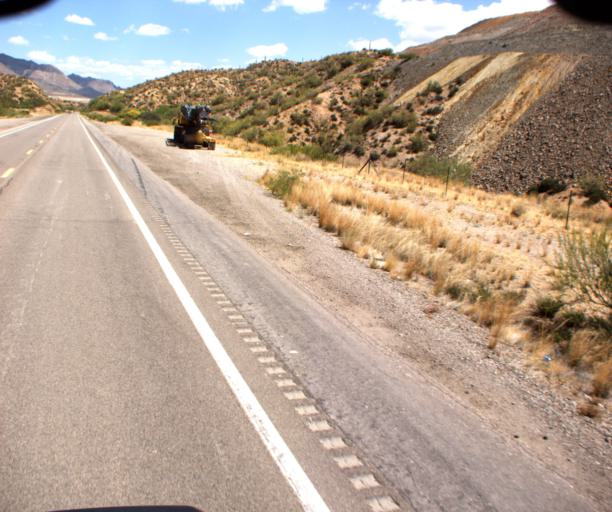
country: US
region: Arizona
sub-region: Pinal County
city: Kearny
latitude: 33.1499
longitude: -110.9938
